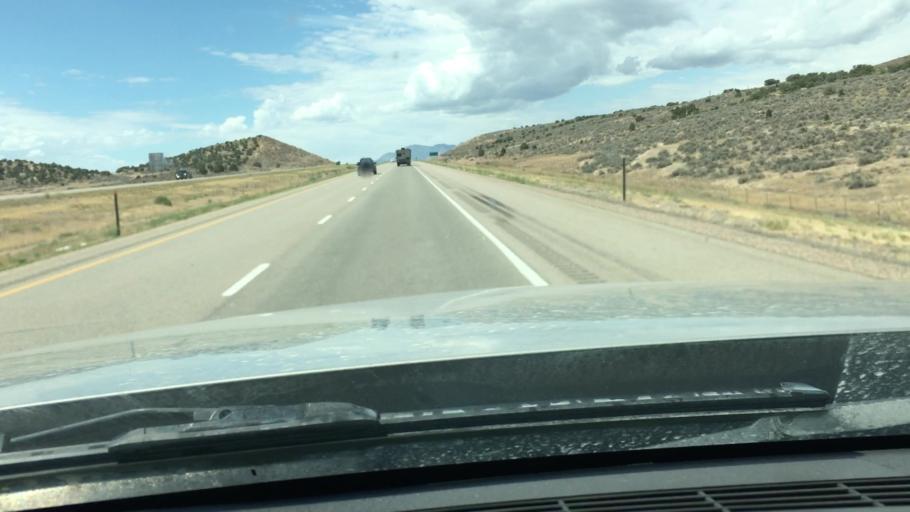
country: US
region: Utah
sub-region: Juab County
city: Nephi
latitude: 39.4769
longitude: -111.9865
